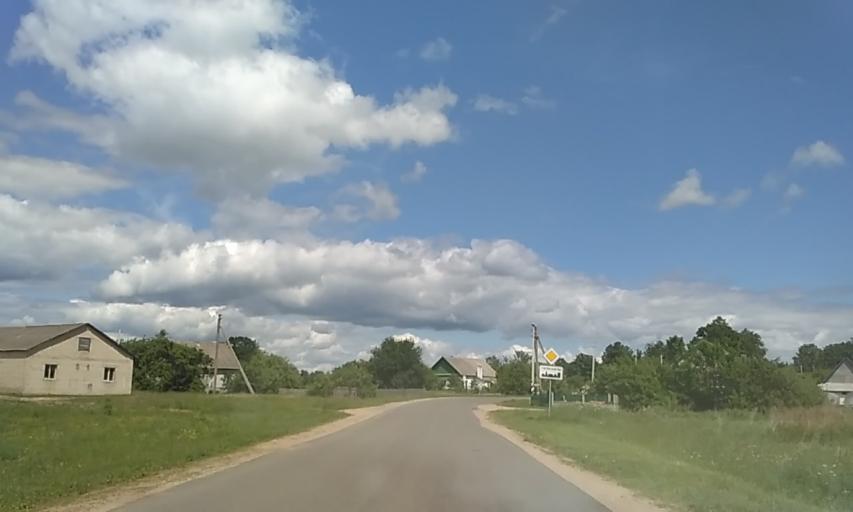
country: BY
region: Minsk
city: Krupki
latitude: 54.3618
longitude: 29.1032
